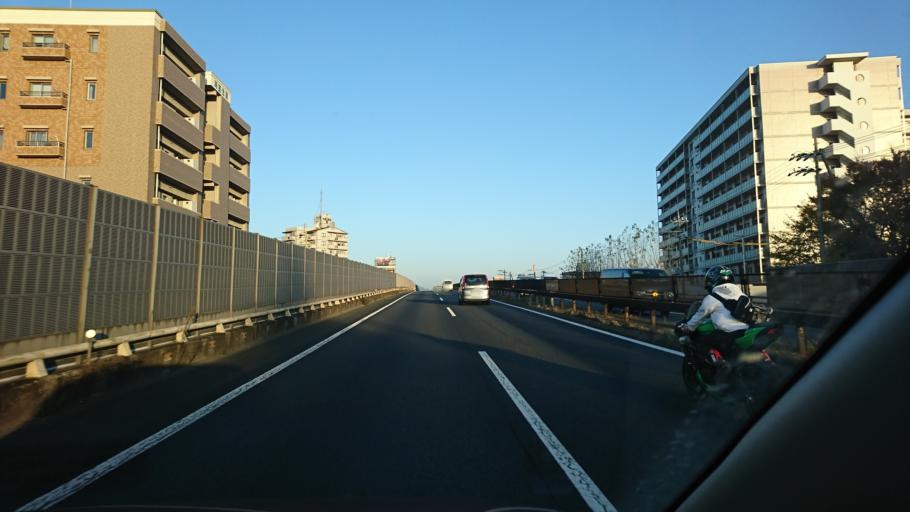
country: JP
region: Hyogo
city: Kakogawacho-honmachi
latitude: 34.7480
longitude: 134.8700
